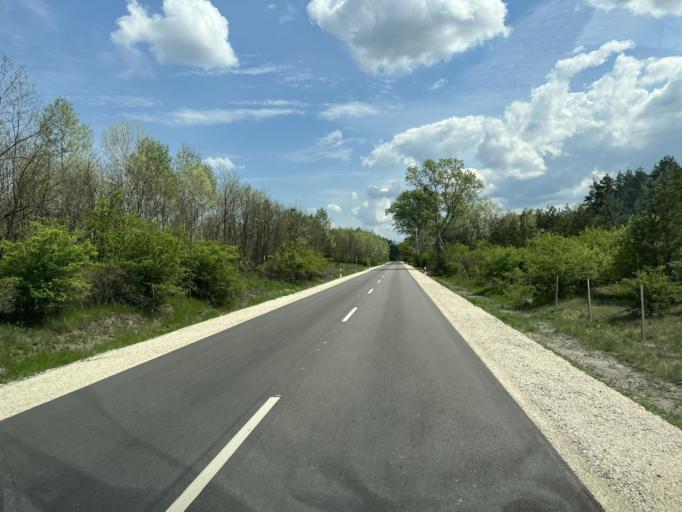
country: HU
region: Pest
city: Csemo
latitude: 47.0865
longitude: 19.6591
